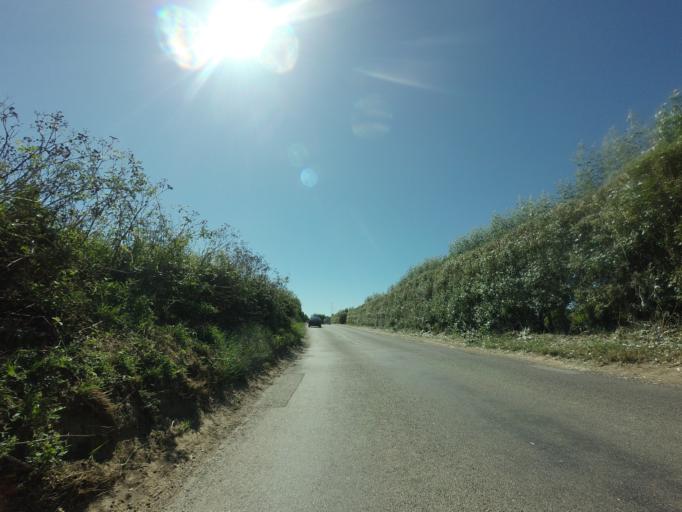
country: GB
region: England
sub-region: Kent
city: Ash
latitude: 51.2809
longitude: 1.2602
